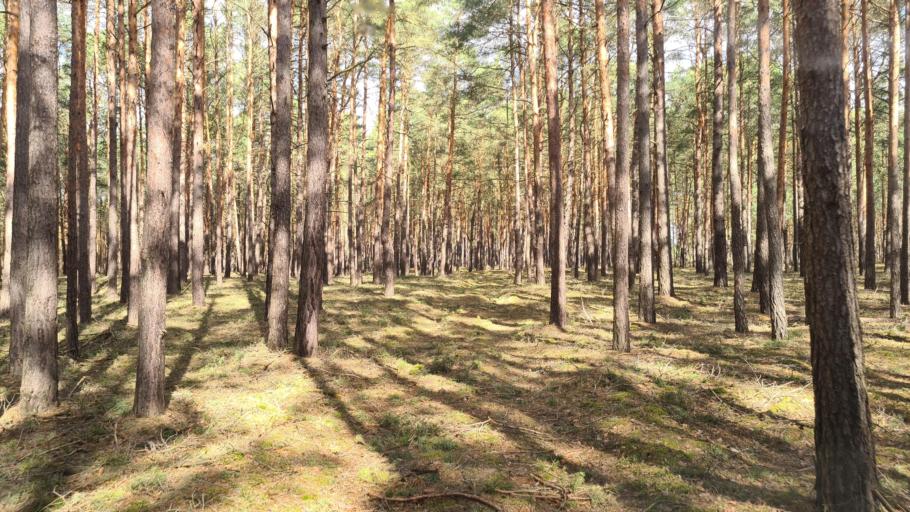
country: DE
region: Brandenburg
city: Bruck
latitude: 52.1656
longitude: 12.7143
